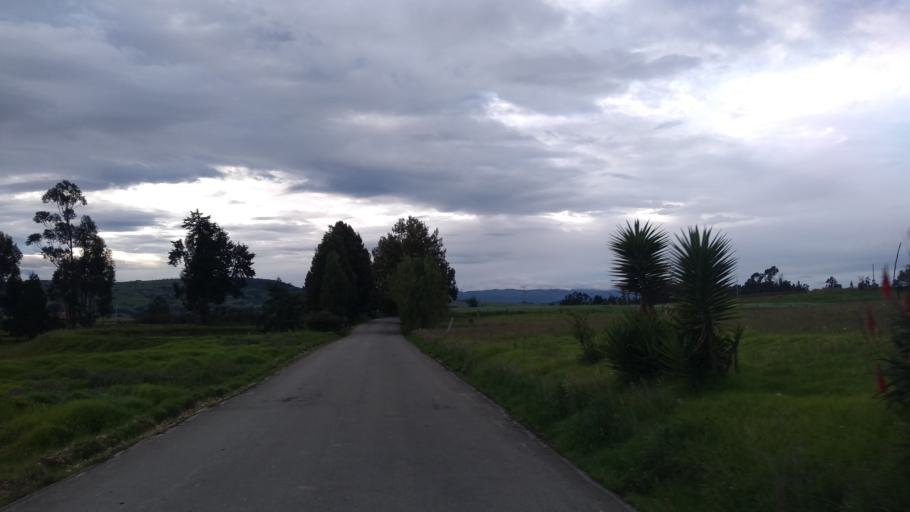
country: CO
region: Boyaca
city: Toca
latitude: 5.5892
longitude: -73.1813
